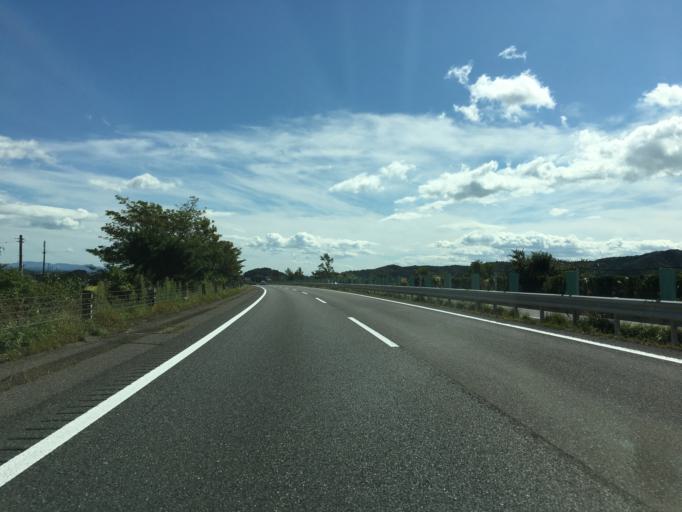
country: JP
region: Fukushima
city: Motomiya
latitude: 37.5300
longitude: 140.3829
